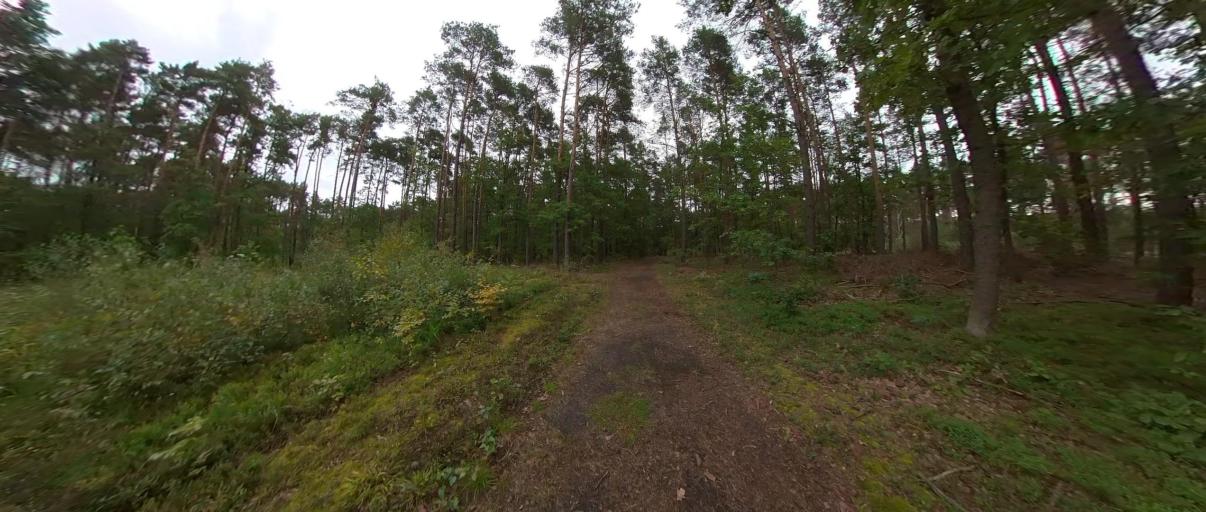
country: PL
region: Masovian Voivodeship
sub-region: Powiat bialobrzeski
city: Bialobrzegi
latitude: 51.6464
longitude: 20.9685
